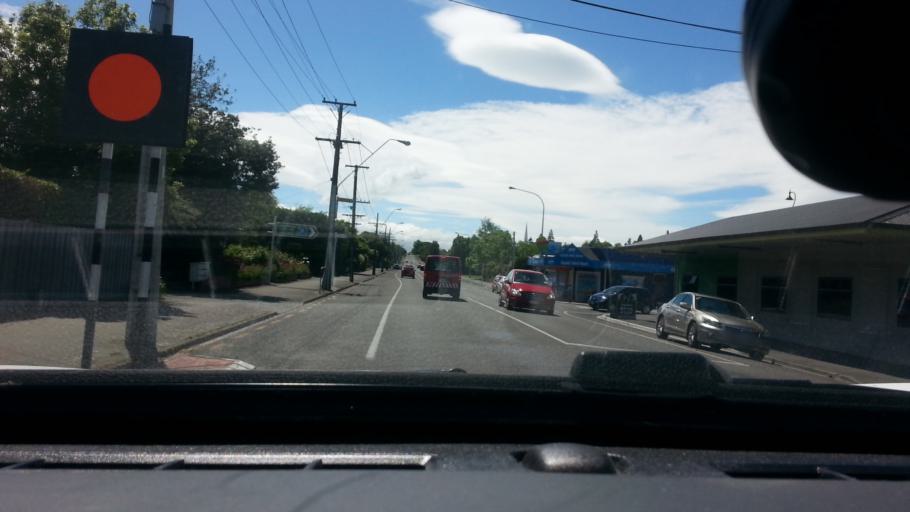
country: NZ
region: Wellington
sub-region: Masterton District
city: Masterton
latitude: -40.9440
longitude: 175.6695
